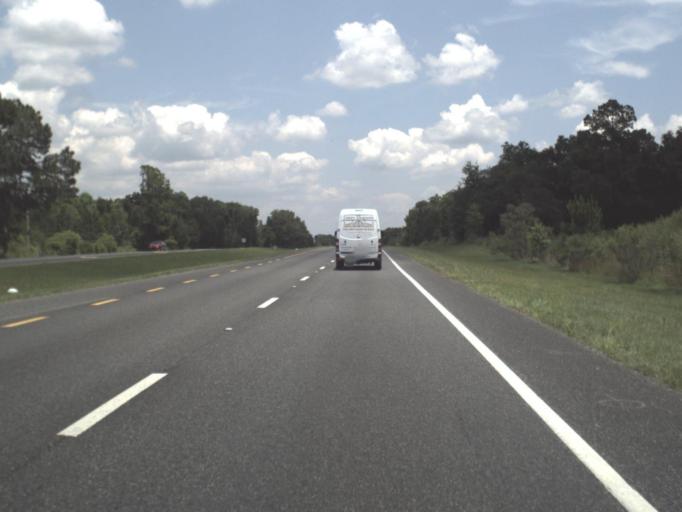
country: US
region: Florida
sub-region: Alachua County
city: Newberry
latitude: 29.6541
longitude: -82.5445
